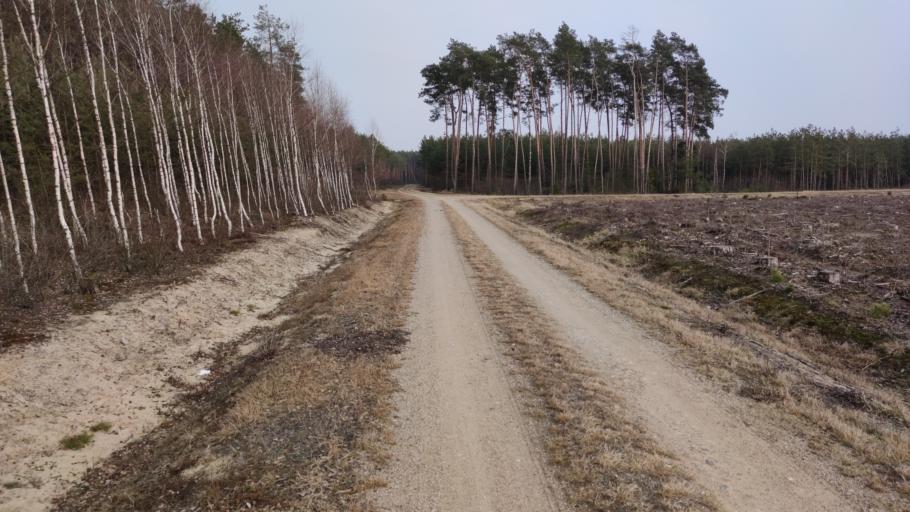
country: PL
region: Masovian Voivodeship
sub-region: Powiat plocki
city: Slubice
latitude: 52.4535
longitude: 19.9561
